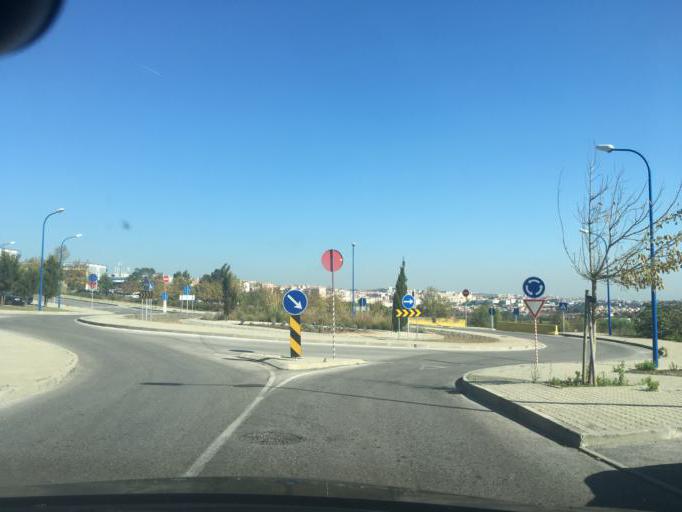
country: PT
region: Lisbon
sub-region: Oeiras
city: Porto Salvo
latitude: 38.7395
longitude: -9.3031
